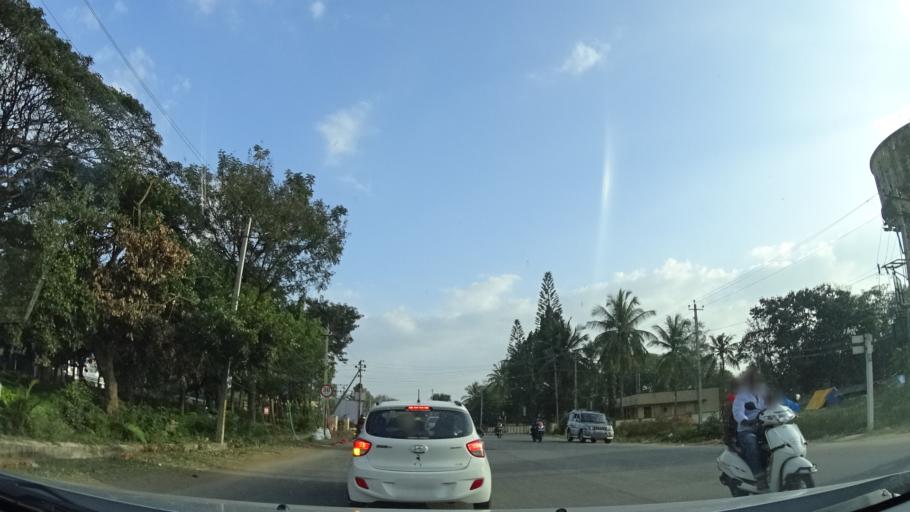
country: IN
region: Karnataka
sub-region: Mandya
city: Malavalli
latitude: 12.3786
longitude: 77.0630
